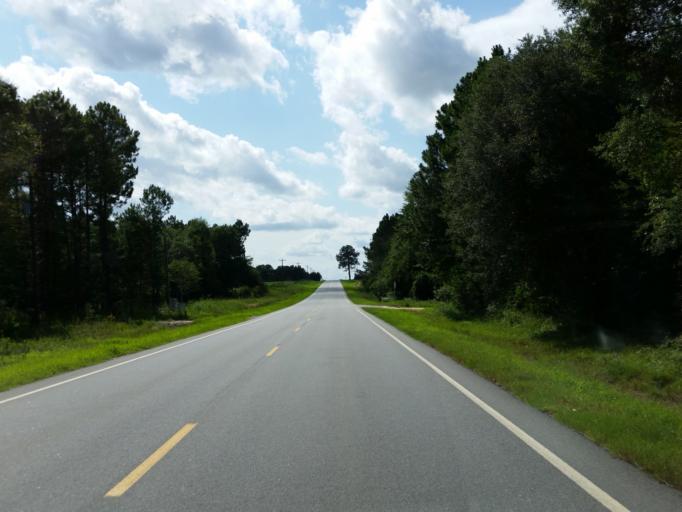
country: US
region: Georgia
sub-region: Turner County
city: Ashburn
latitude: 31.6383
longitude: -83.5209
